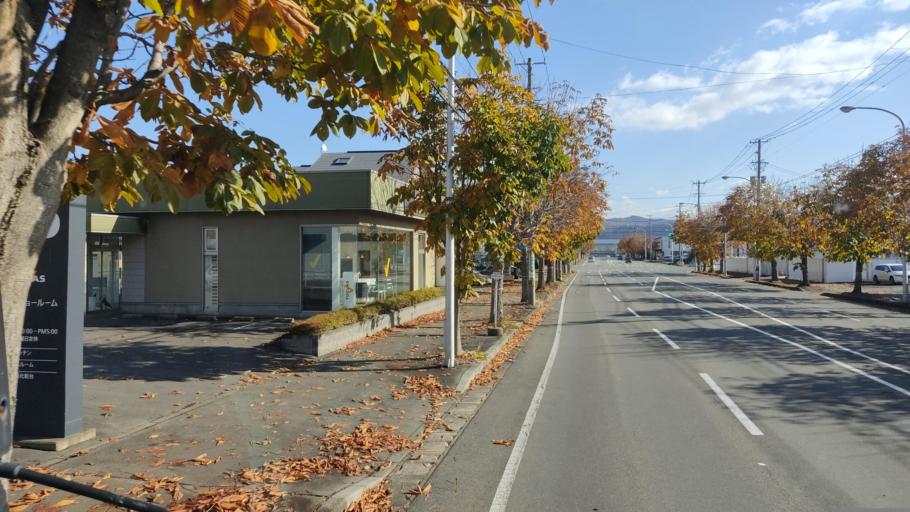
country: JP
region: Iwate
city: Morioka-shi
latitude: 39.6846
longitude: 141.1419
